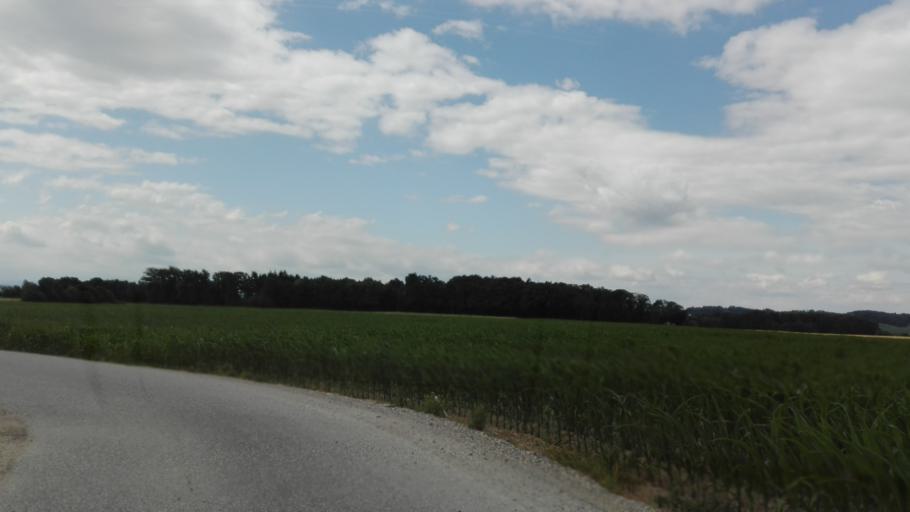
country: AT
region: Upper Austria
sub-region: Politischer Bezirk Perg
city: Perg
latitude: 48.2570
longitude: 14.5666
